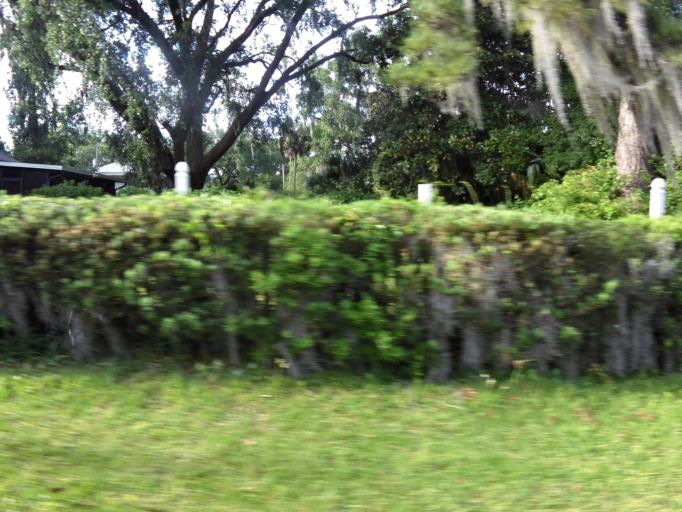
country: US
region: Florida
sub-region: Duval County
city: Jacksonville
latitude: 30.3651
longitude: -81.6557
